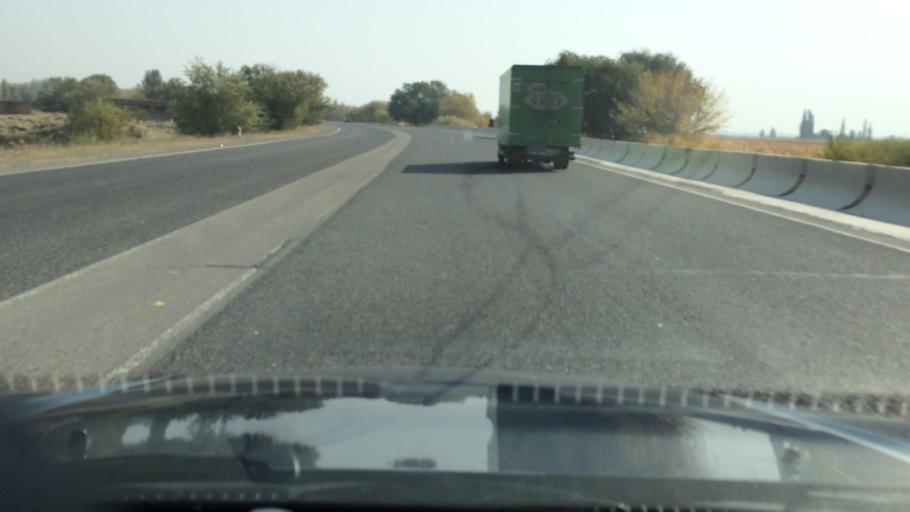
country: KG
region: Chuy
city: Ivanovka
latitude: 42.9406
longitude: 74.9696
